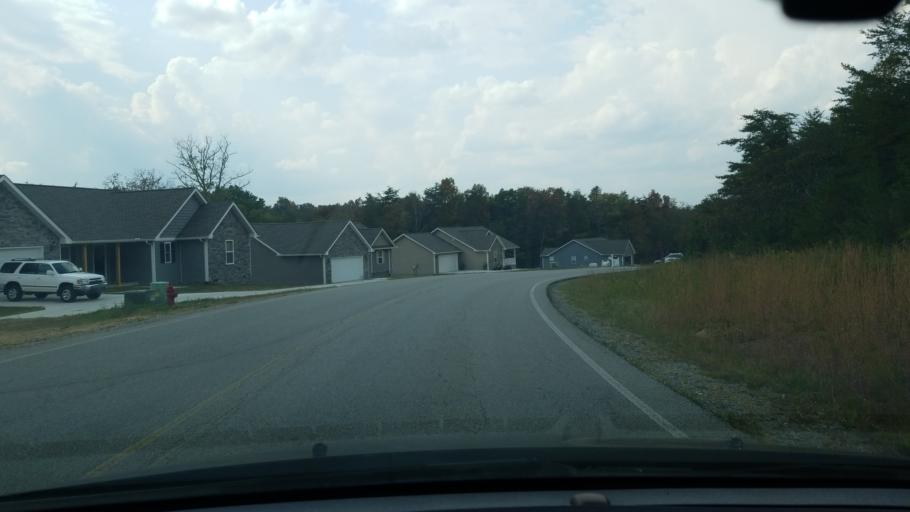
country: US
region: Tennessee
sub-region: Cumberland County
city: Crossville
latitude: 35.9469
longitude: -85.0468
